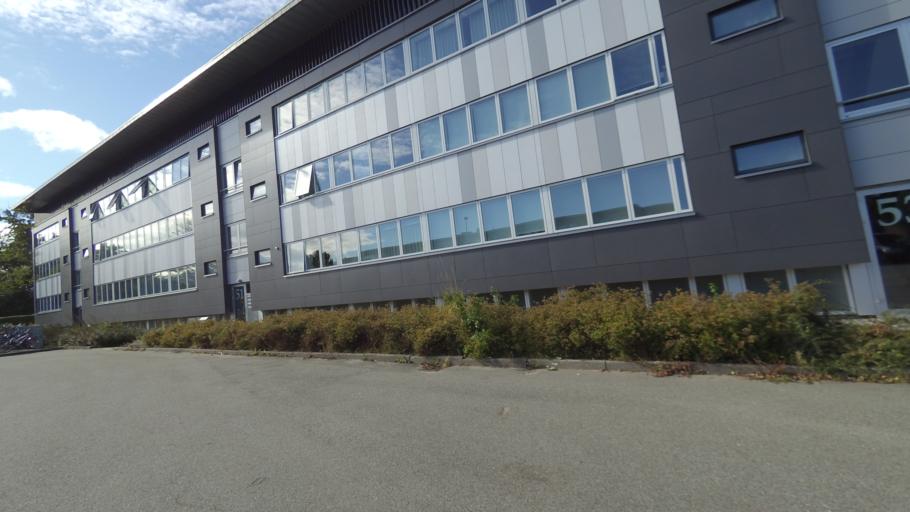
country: DK
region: Central Jutland
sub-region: Arhus Kommune
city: Stavtrup
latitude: 56.1197
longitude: 10.1484
